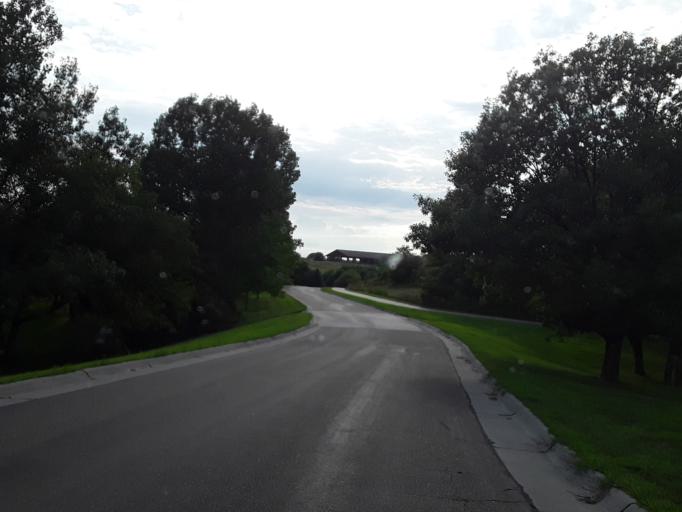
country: US
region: Nebraska
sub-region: Saunders County
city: Ashland
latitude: 41.0231
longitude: -96.3088
